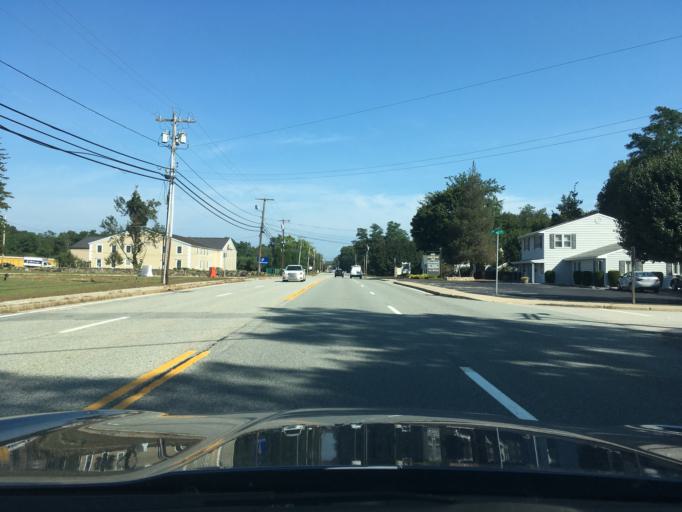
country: US
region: Rhode Island
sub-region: Kent County
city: East Greenwich
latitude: 41.6201
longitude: -71.4913
